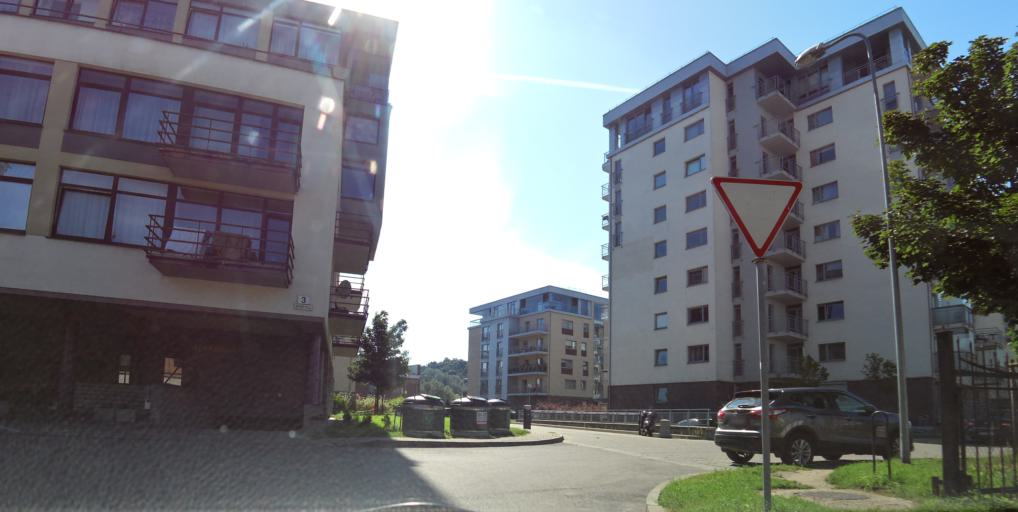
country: LT
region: Vilnius County
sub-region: Vilnius
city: Vilnius
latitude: 54.6937
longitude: 25.2951
